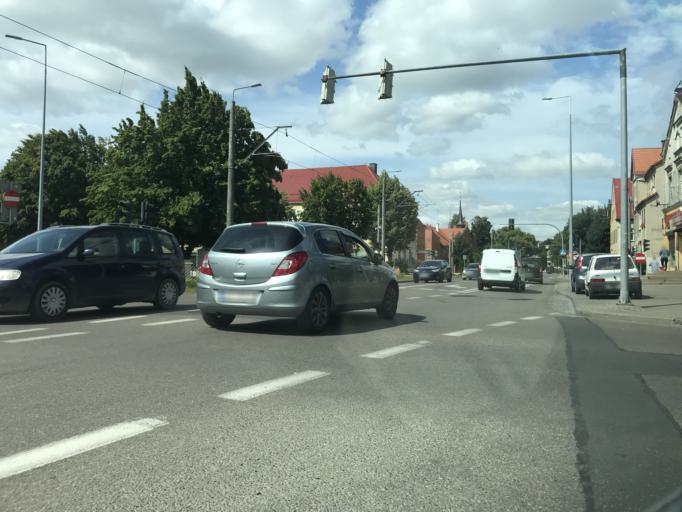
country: PL
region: Warmian-Masurian Voivodeship
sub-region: Powiat elblaski
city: Elblag
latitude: 54.1591
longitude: 19.4191
